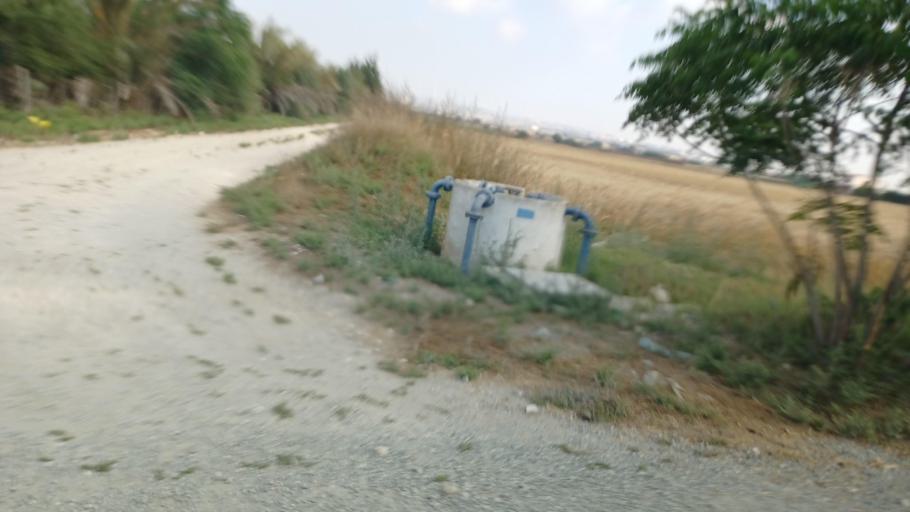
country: CY
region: Larnaka
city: Tersefanou
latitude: 34.8291
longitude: 33.5544
